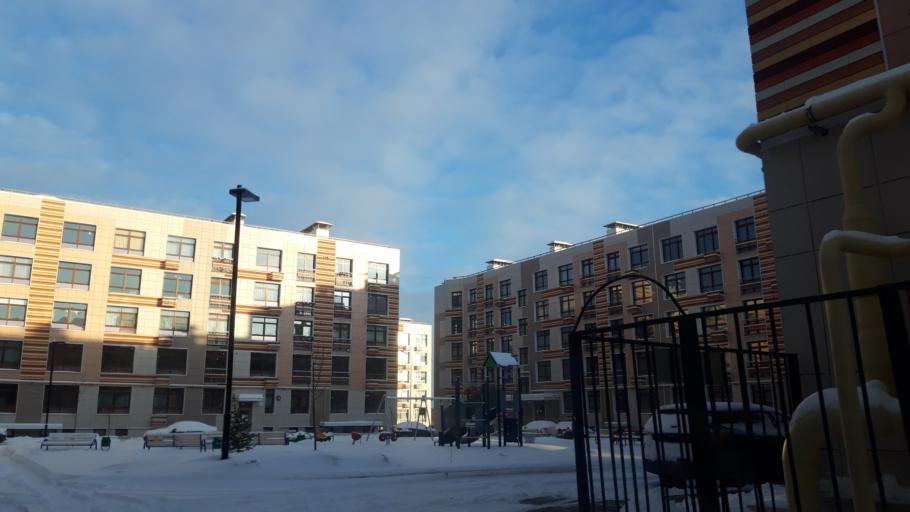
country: RU
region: Moskovskaya
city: Novopodrezkovo
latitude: 55.9074
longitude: 37.3290
